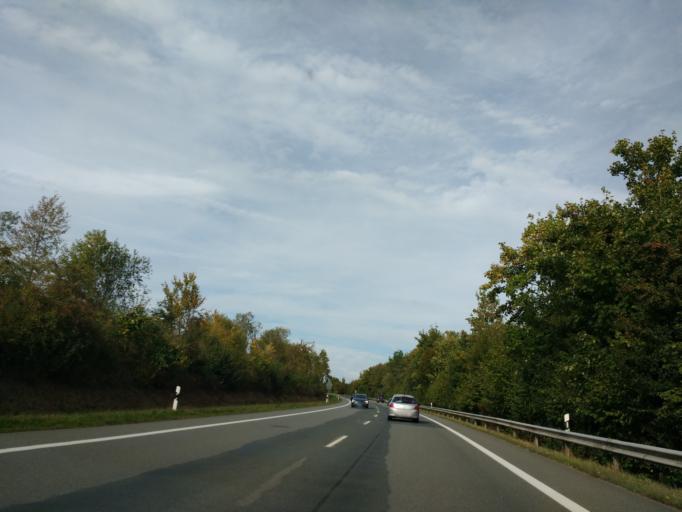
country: DE
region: North Rhine-Westphalia
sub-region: Regierungsbezirk Detmold
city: Steinheim
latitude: 51.8606
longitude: 9.1045
